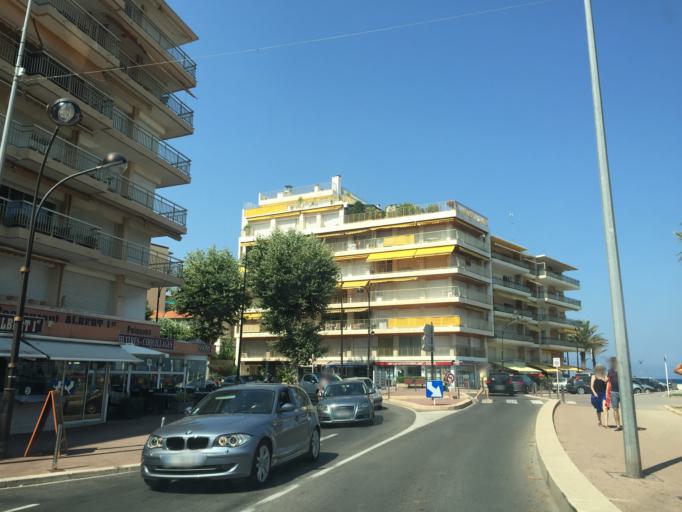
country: FR
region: Provence-Alpes-Cote d'Azur
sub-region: Departement des Alpes-Maritimes
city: Antibes
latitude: 43.5762
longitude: 7.1249
